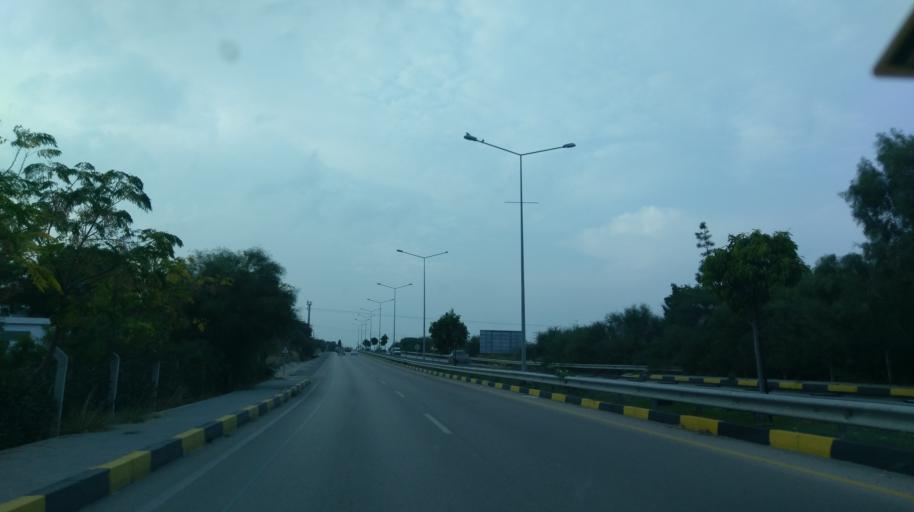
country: CY
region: Keryneia
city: Kyrenia
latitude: 35.3353
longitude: 33.2611
